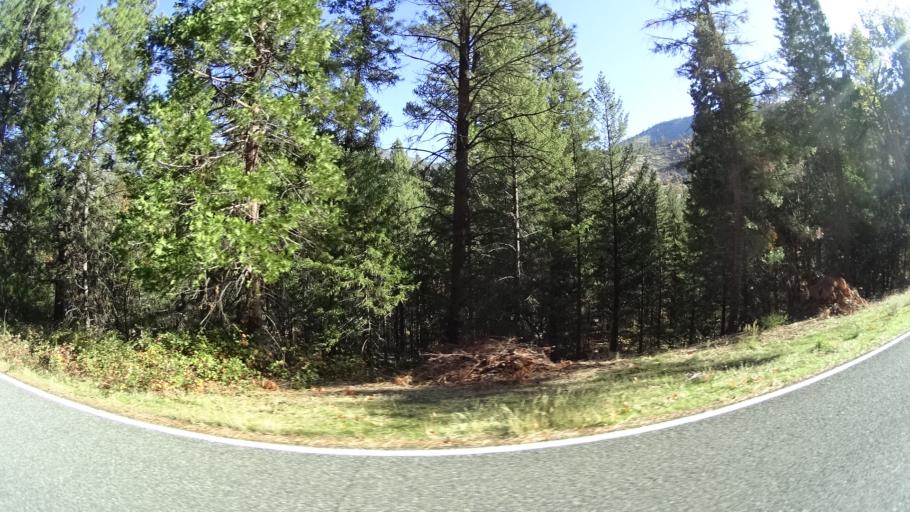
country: US
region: California
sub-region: Siskiyou County
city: Yreka
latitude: 41.8932
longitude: -122.8241
